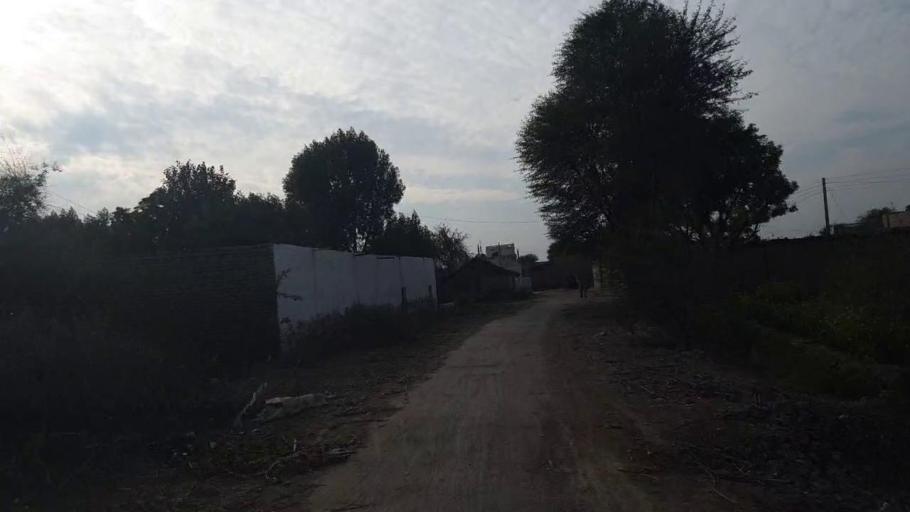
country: PK
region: Sindh
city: Shahpur Chakar
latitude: 26.0531
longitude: 68.5667
